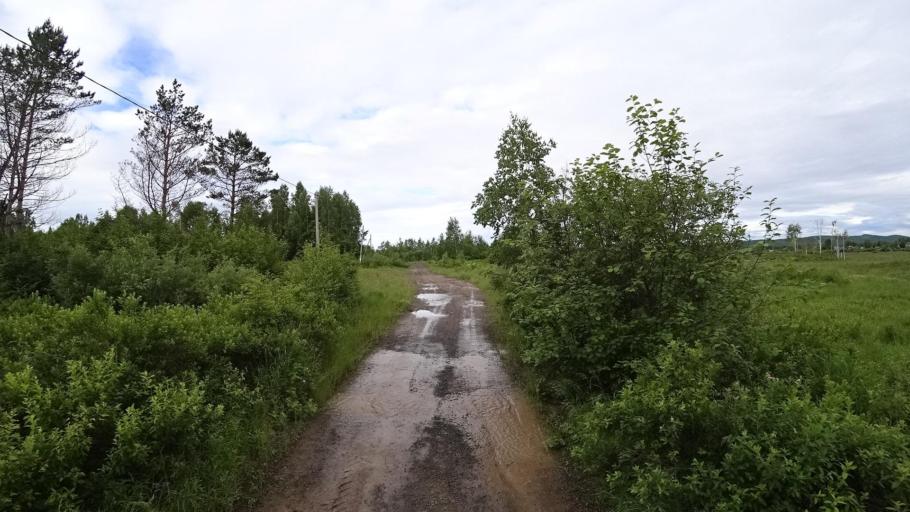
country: RU
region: Khabarovsk Krai
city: Amursk
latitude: 49.8950
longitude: 136.1462
